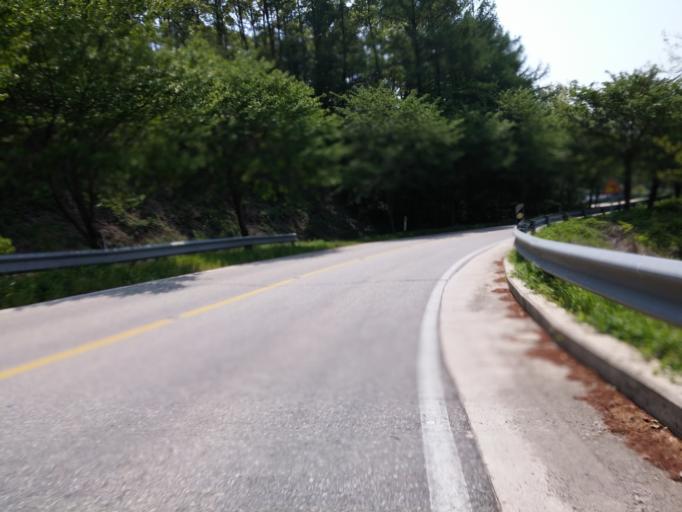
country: KR
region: Daejeon
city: Sintansin
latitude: 36.4346
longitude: 127.5633
